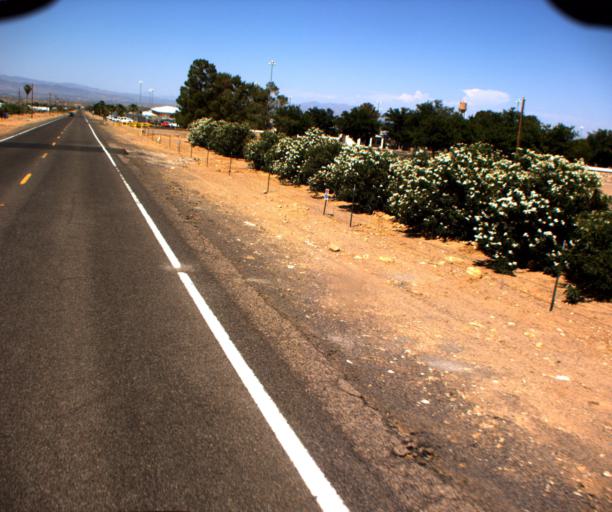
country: US
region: Arizona
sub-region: Graham County
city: Swift Trail Junction
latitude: 32.7158
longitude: -109.7284
